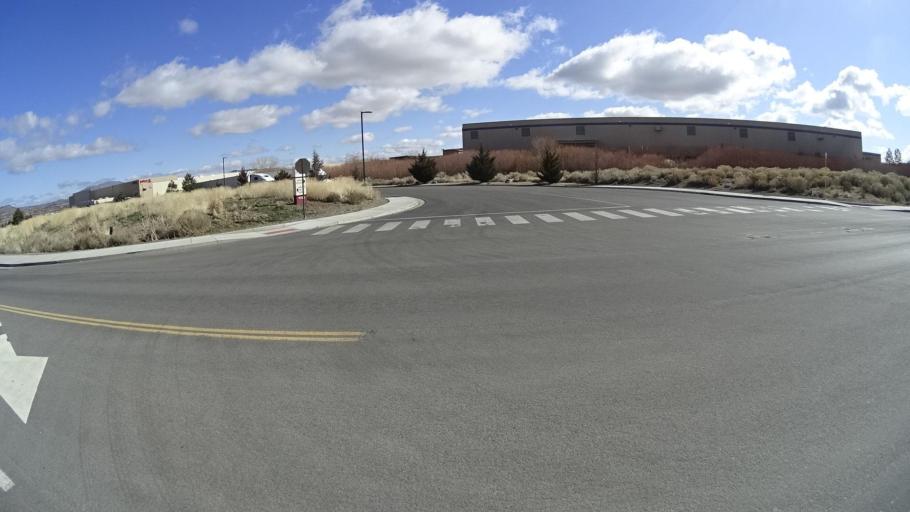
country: US
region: Nevada
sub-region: Washoe County
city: Cold Springs
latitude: 39.6344
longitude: -119.9185
